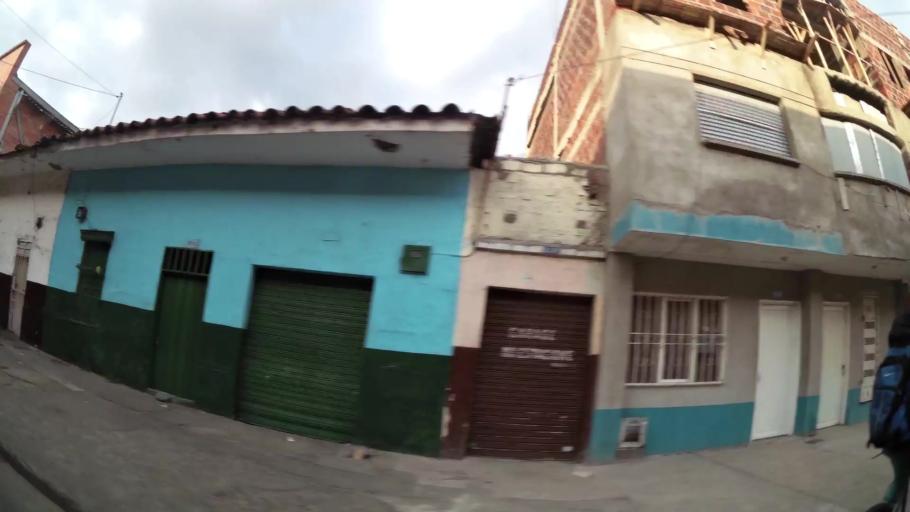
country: CO
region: Valle del Cauca
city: Cali
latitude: 3.4514
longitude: -76.5206
